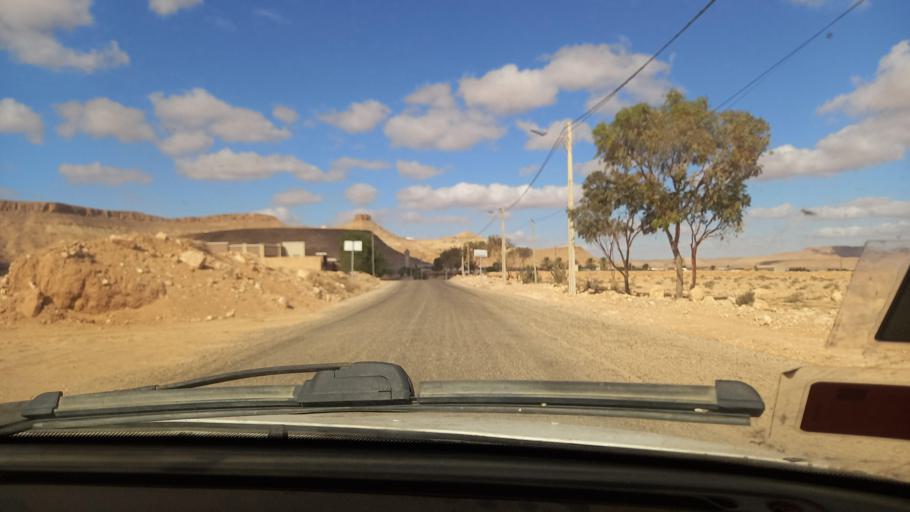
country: TN
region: Tataouine
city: Tataouine
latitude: 32.9788
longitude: 10.2736
